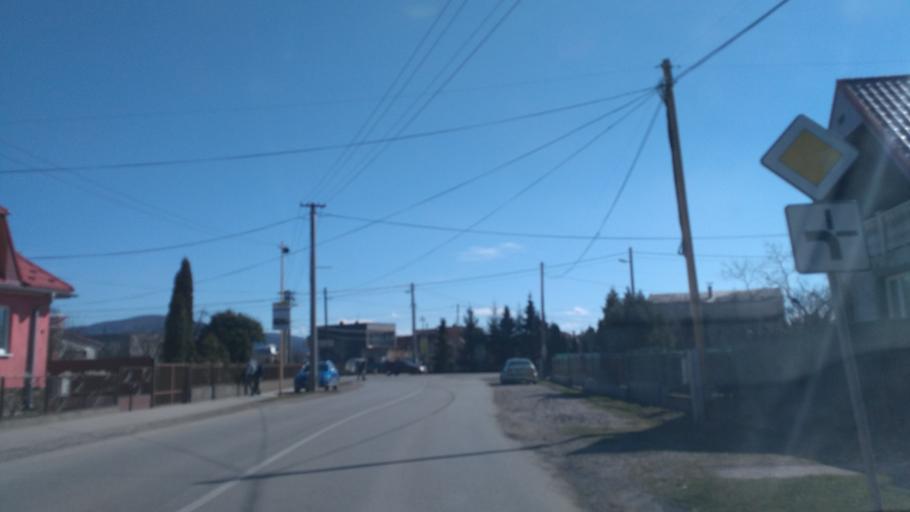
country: SK
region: Kosicky
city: Kosice
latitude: 48.6077
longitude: 21.3222
